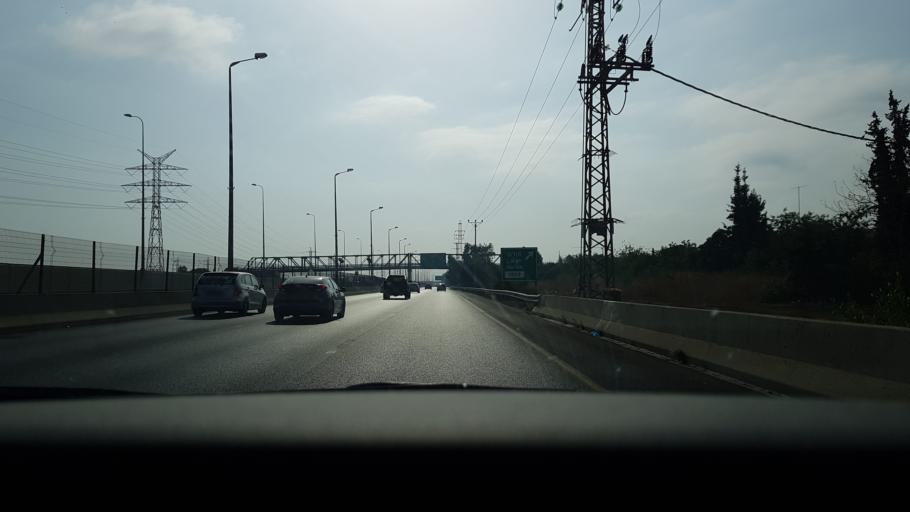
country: IL
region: Tel Aviv
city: Azor
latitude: 32.0303
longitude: 34.8043
